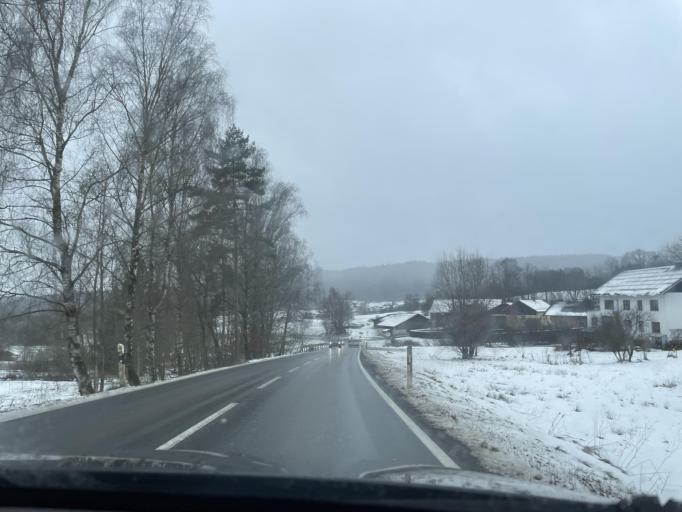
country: DE
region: Bavaria
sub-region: Upper Palatinate
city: Rimbach
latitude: 49.2221
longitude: 12.8469
